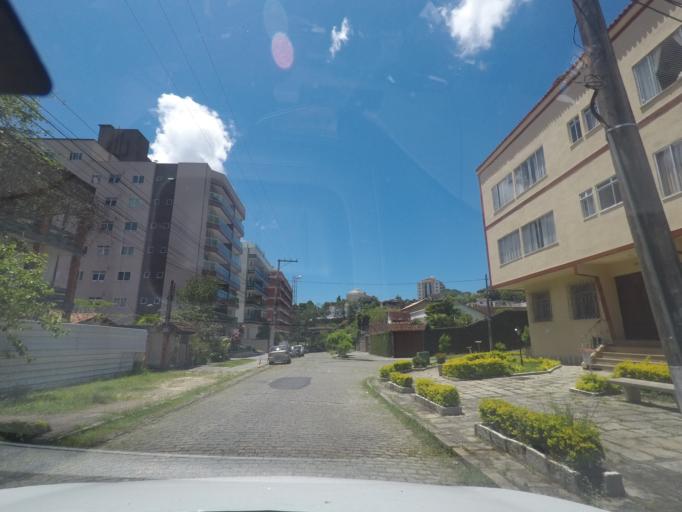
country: BR
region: Rio de Janeiro
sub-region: Teresopolis
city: Teresopolis
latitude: -22.4298
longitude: -42.9825
